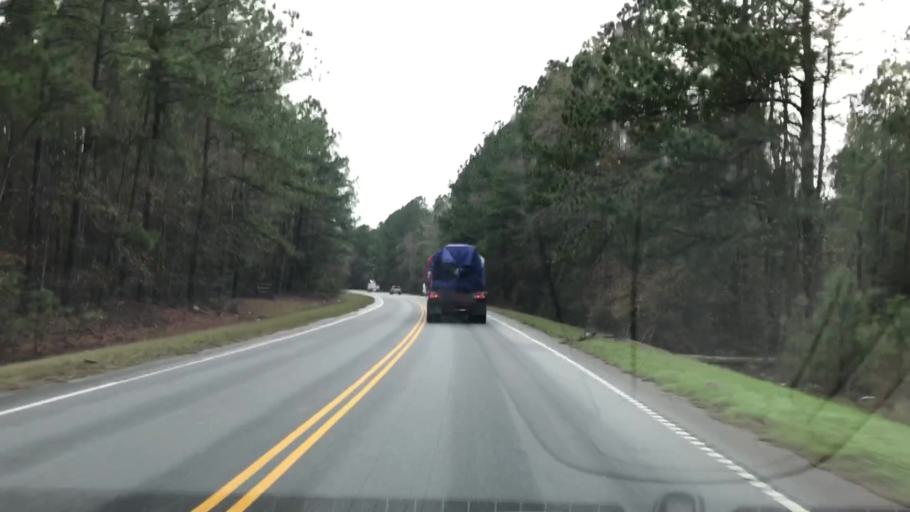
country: US
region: South Carolina
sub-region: Berkeley County
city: Bonneau Beach
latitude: 33.2566
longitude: -79.9348
